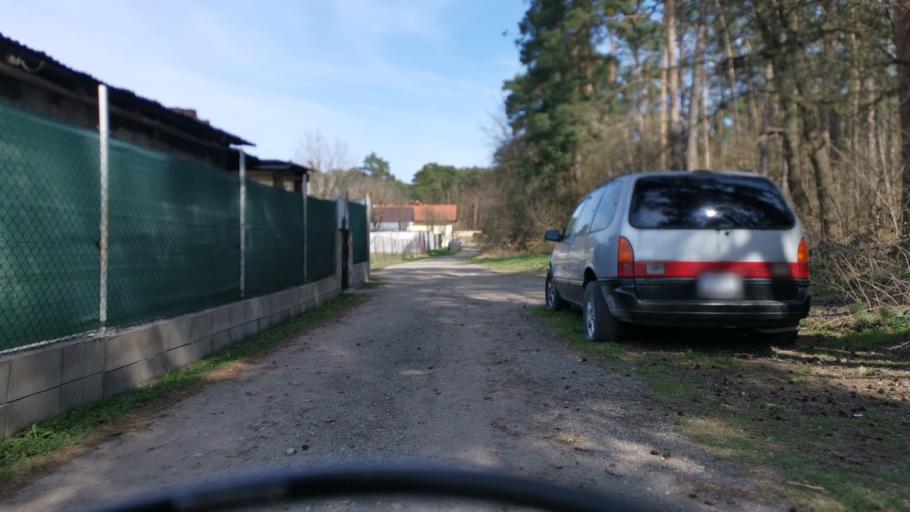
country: SK
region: Trnavsky
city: Gbely
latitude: 48.7096
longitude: 17.0949
